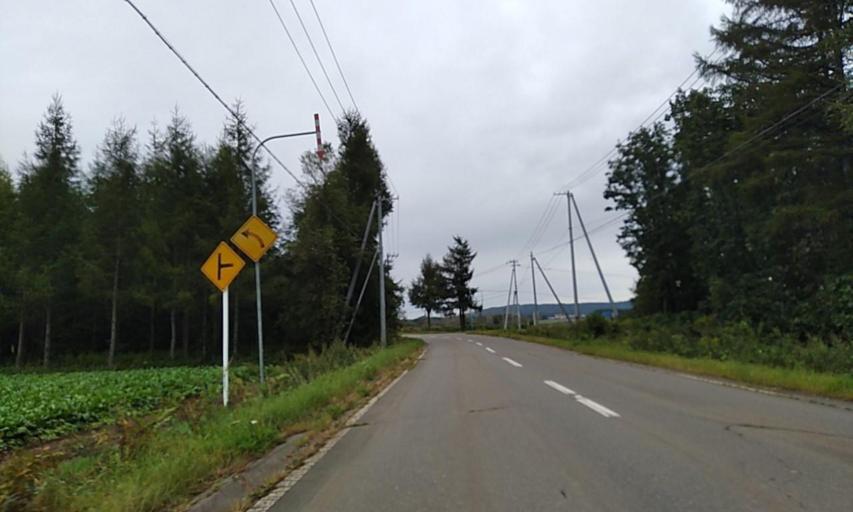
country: JP
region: Hokkaido
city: Obihiro
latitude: 42.6175
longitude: 143.2585
